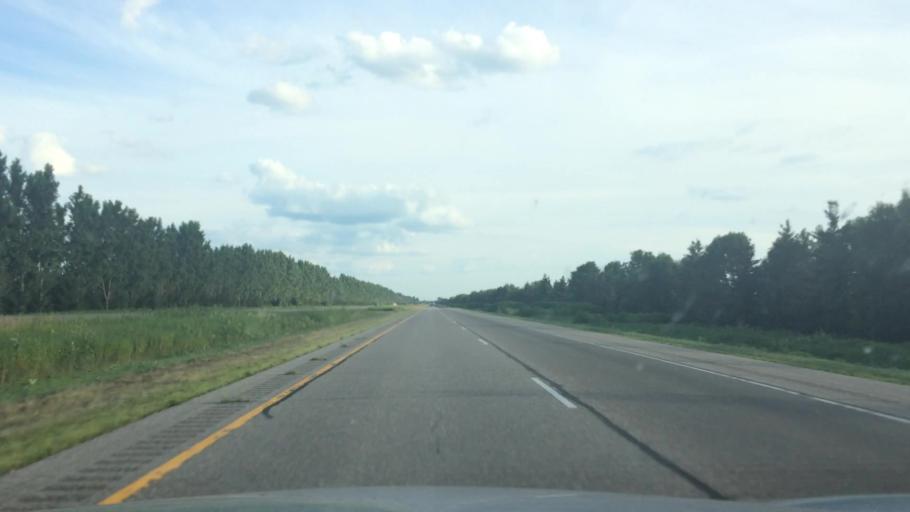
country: US
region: Wisconsin
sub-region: Portage County
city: Plover
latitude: 44.3576
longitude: -89.5211
